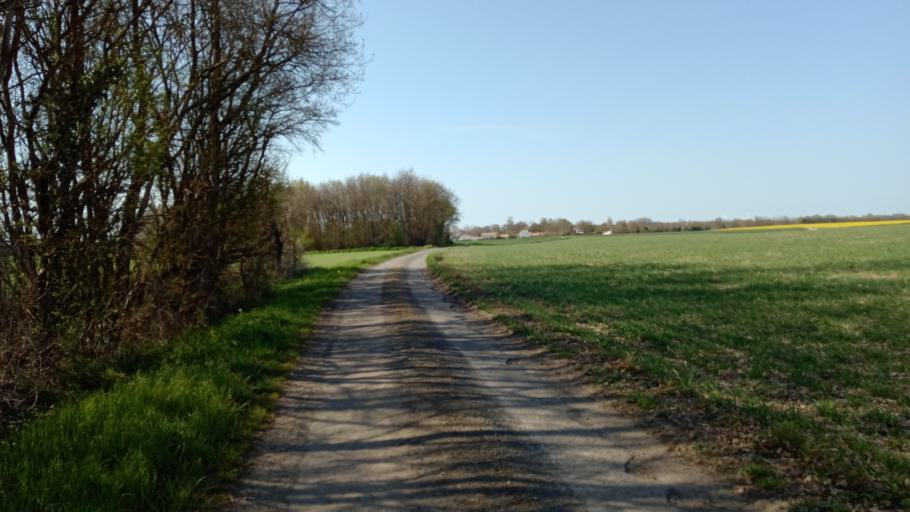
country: FR
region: Poitou-Charentes
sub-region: Departement de la Charente-Maritime
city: Verines
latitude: 46.1622
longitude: -0.9395
